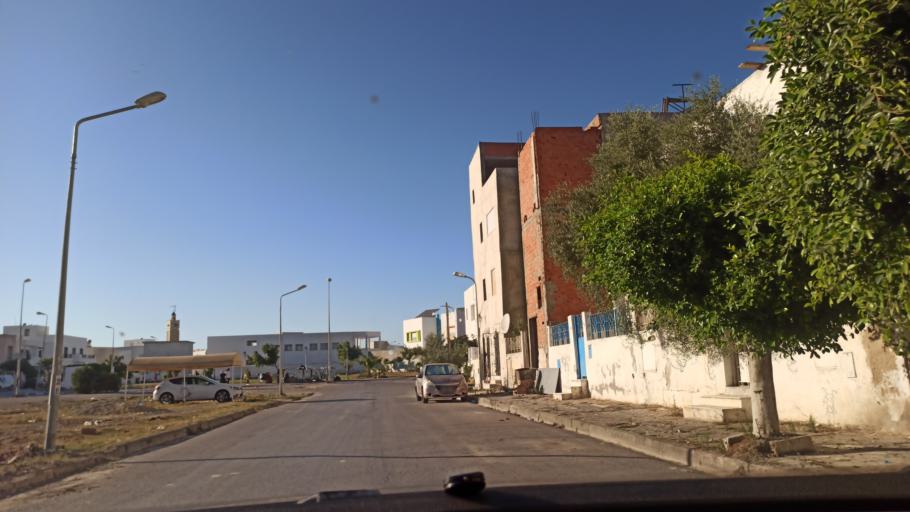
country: TN
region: Tunis
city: La Goulette
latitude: 36.8521
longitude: 10.2566
